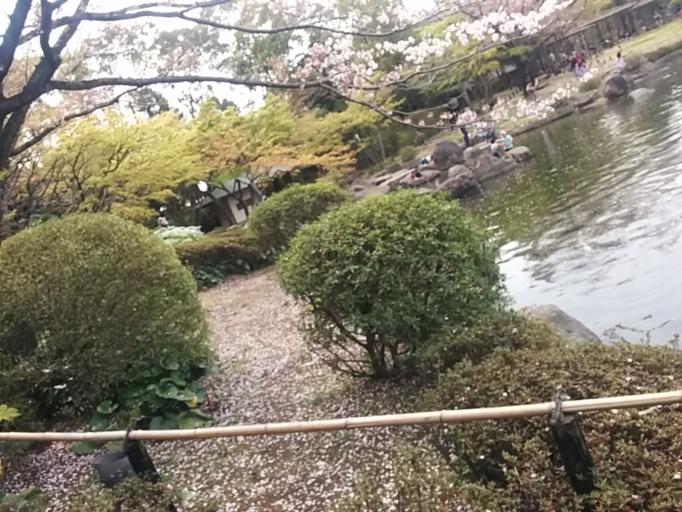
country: JP
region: Tokyo
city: Urayasu
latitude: 35.6716
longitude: 139.8592
